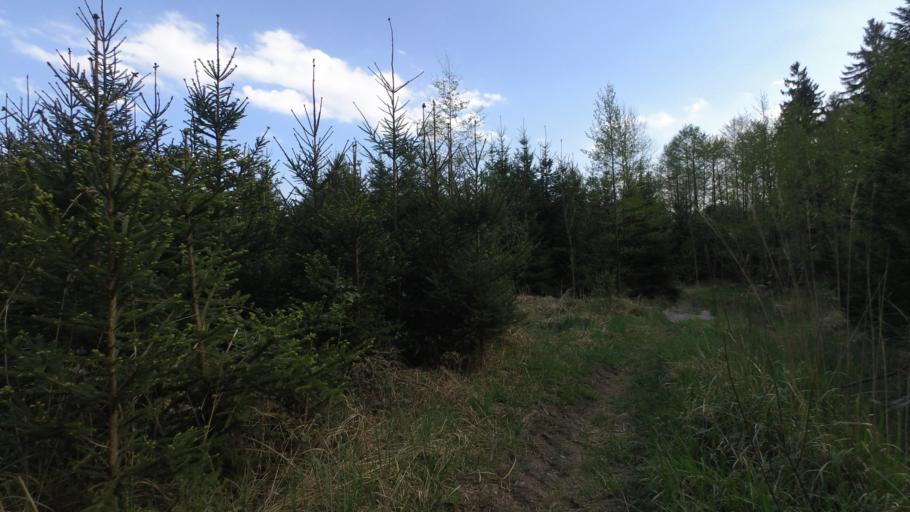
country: DE
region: Bavaria
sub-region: Upper Bavaria
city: Chieming
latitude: 47.9167
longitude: 12.5101
